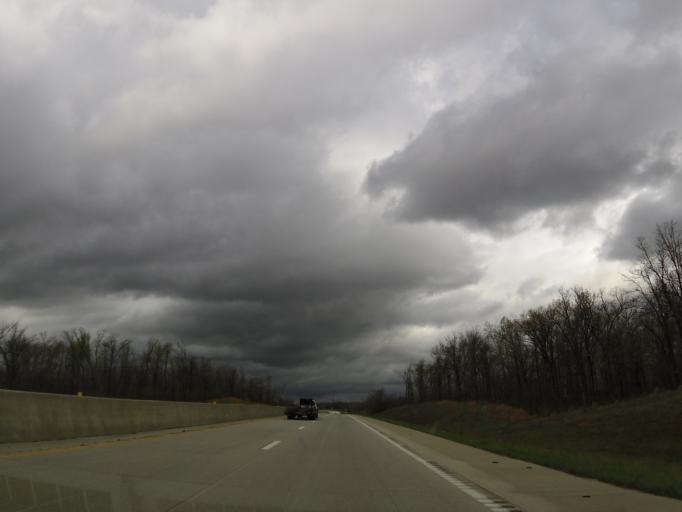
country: US
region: Missouri
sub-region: Butler County
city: Poplar Bluff
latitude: 36.6699
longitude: -90.4969
